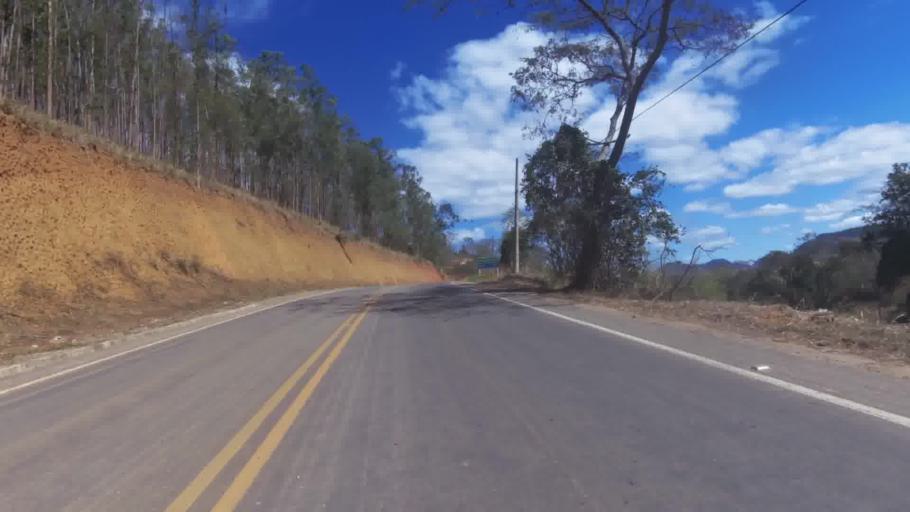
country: BR
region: Espirito Santo
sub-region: Cachoeiro De Itapemirim
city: Cachoeiro de Itapemirim
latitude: -20.9135
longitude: -41.2016
